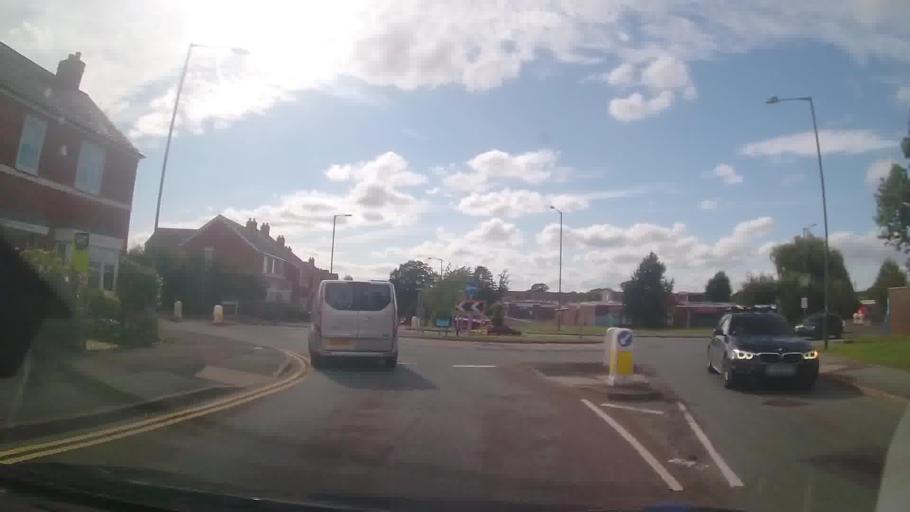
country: GB
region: England
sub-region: Shropshire
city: Great Hanwood
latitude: 52.7068
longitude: -2.7920
